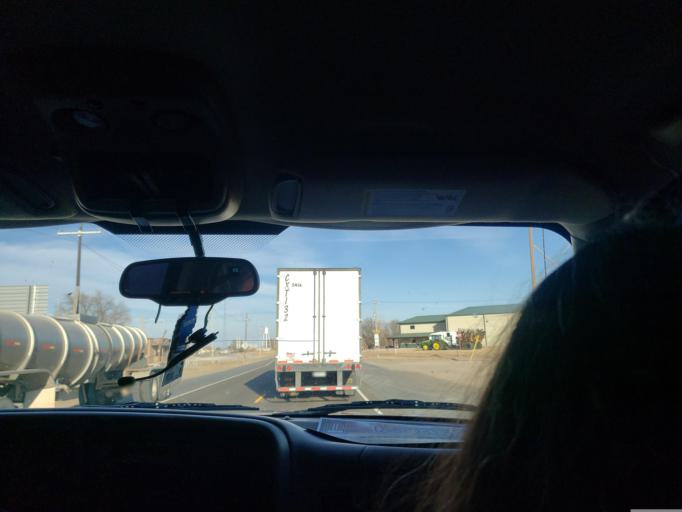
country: US
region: Oklahoma
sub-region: Texas County
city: Goodwell
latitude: 36.4995
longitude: -101.7881
